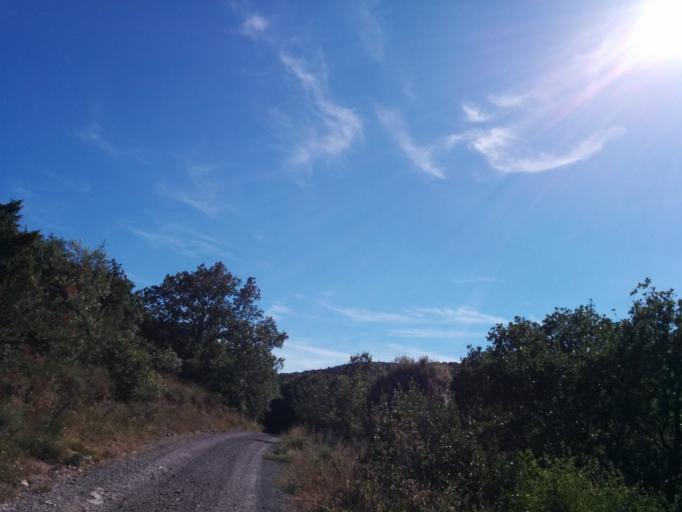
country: FR
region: Languedoc-Roussillon
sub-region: Departement du Gard
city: Saint-Christol-les-Ales
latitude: 44.0963
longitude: 4.0575
